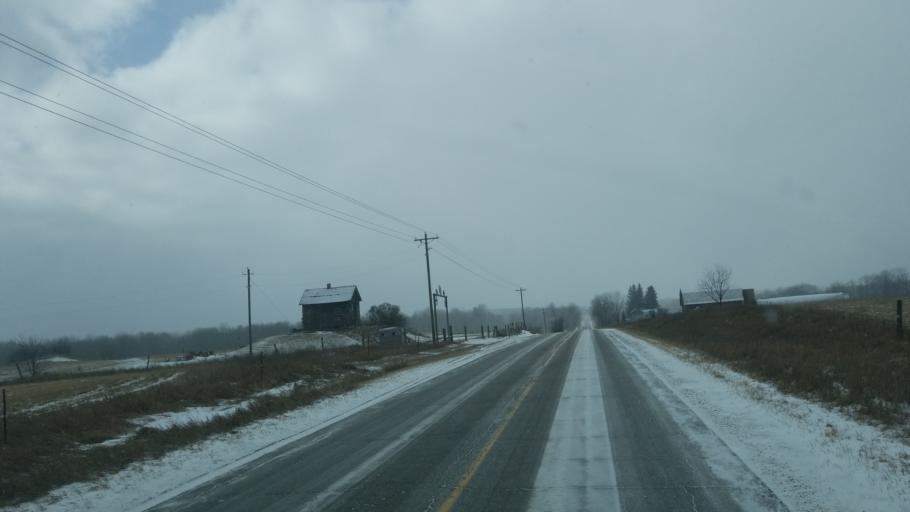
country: US
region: Michigan
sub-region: Osceola County
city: Evart
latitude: 44.0303
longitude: -85.2108
